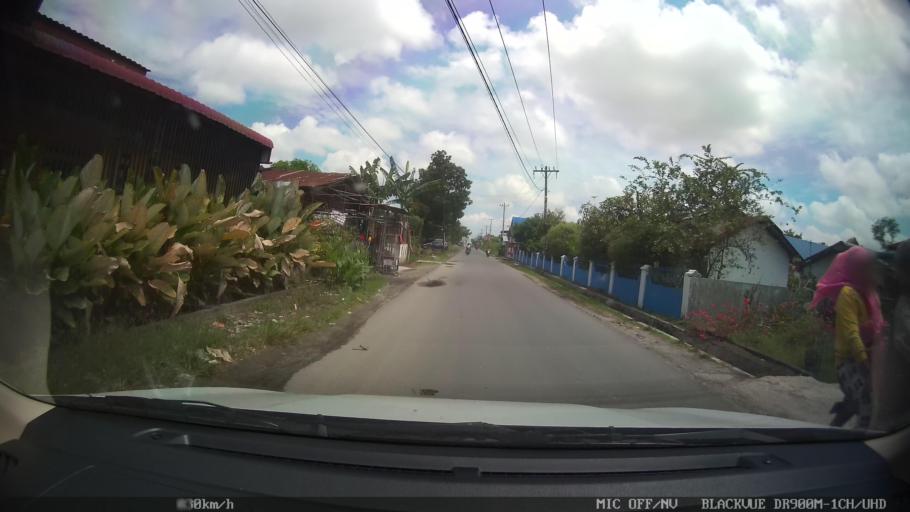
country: ID
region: North Sumatra
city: Percut
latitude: 3.6109
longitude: 98.7815
